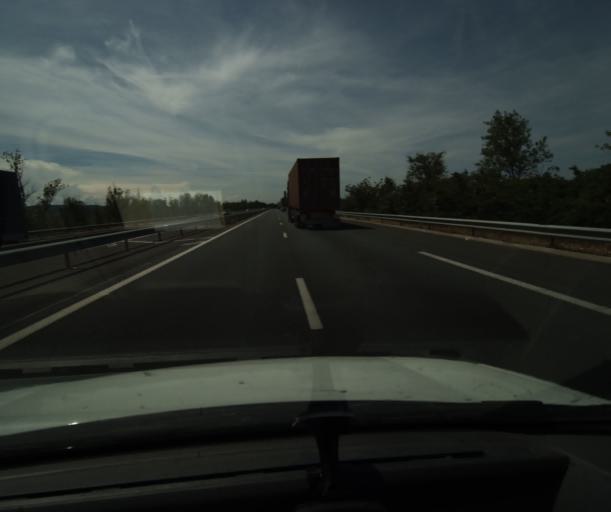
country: FR
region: Languedoc-Roussillon
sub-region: Departement de l'Aude
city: Lavalette
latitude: 43.2034
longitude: 2.2614
